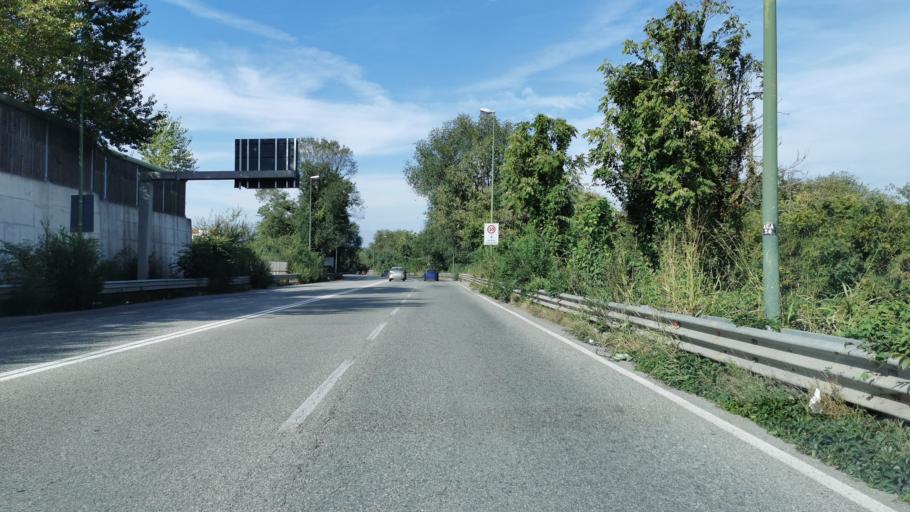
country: IT
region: Piedmont
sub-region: Provincia di Torino
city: Venaria Reale
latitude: 45.1152
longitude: 7.6623
